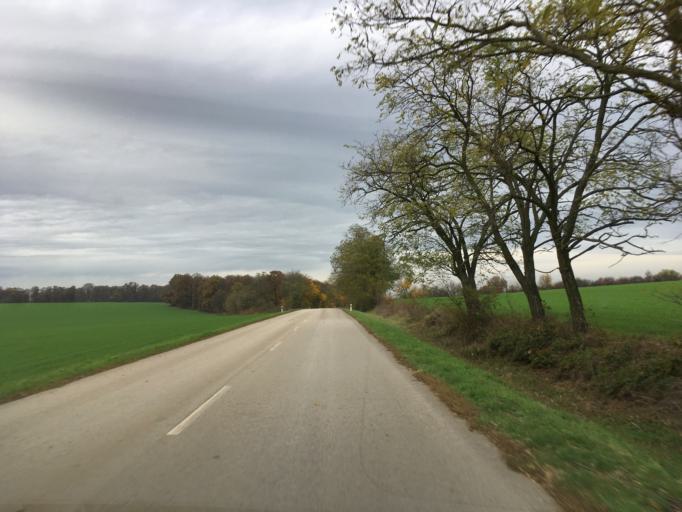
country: SK
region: Nitriansky
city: Svodin
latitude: 48.0297
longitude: 18.3958
